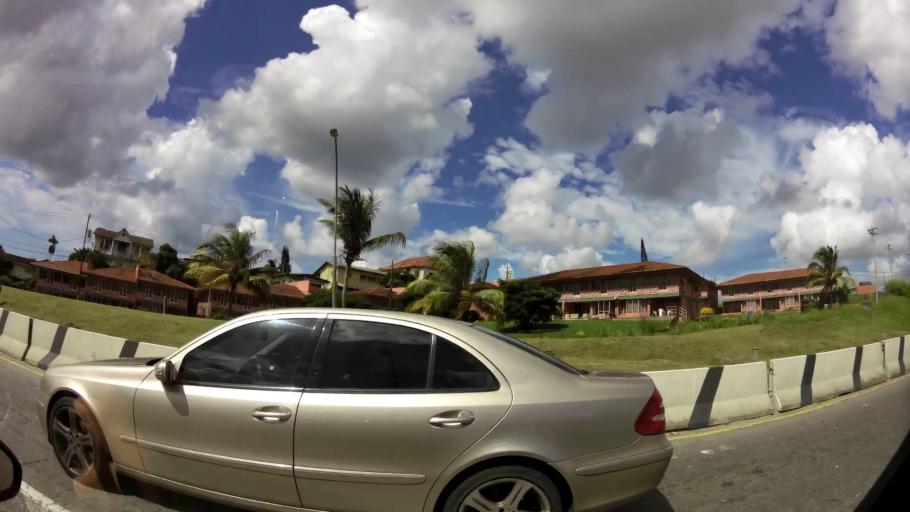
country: TT
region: City of San Fernando
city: San Fernando
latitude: 10.2575
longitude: -61.4716
